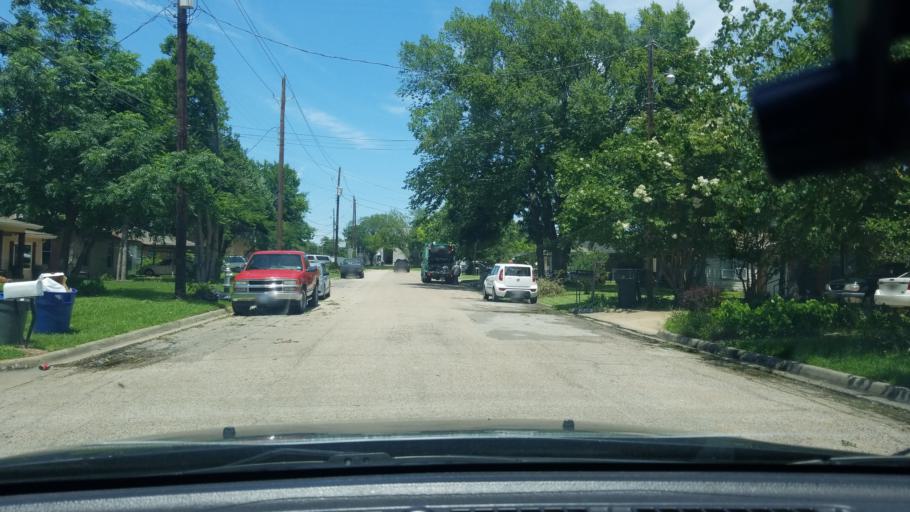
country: US
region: Texas
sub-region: Dallas County
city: Mesquite
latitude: 32.7907
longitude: -96.6162
